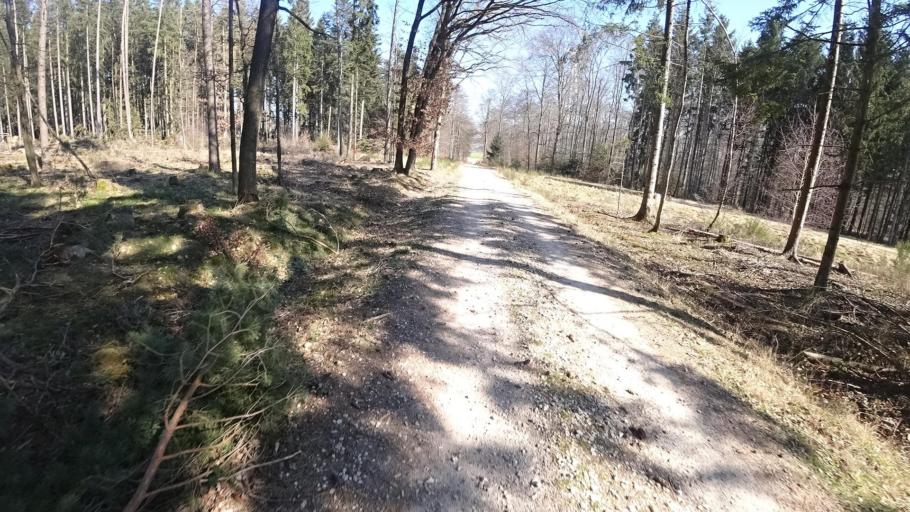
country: DE
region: Rheinland-Pfalz
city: Steinbach
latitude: 50.0342
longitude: 7.6058
